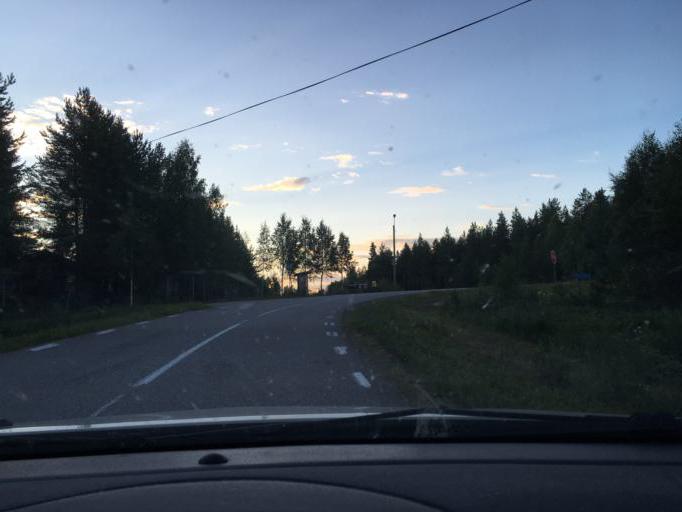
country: SE
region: Norrbotten
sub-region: Kalix Kommun
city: Rolfs
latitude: 65.9044
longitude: 22.9304
